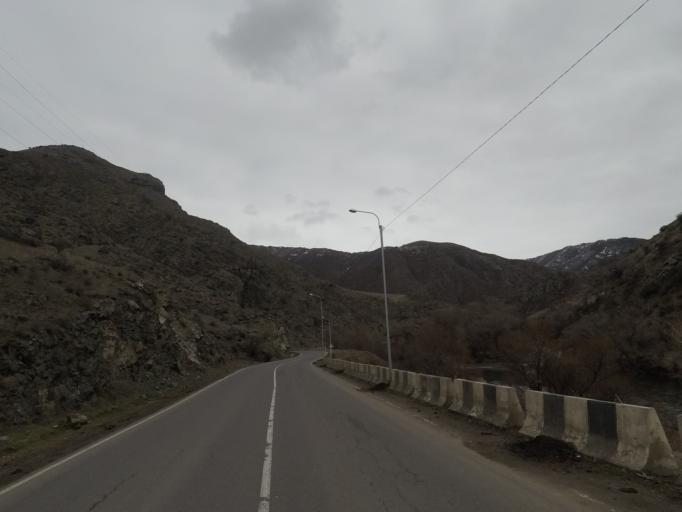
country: GE
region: Samtskhe-Javakheti
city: Aspindza
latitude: 41.5638
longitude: 43.2665
